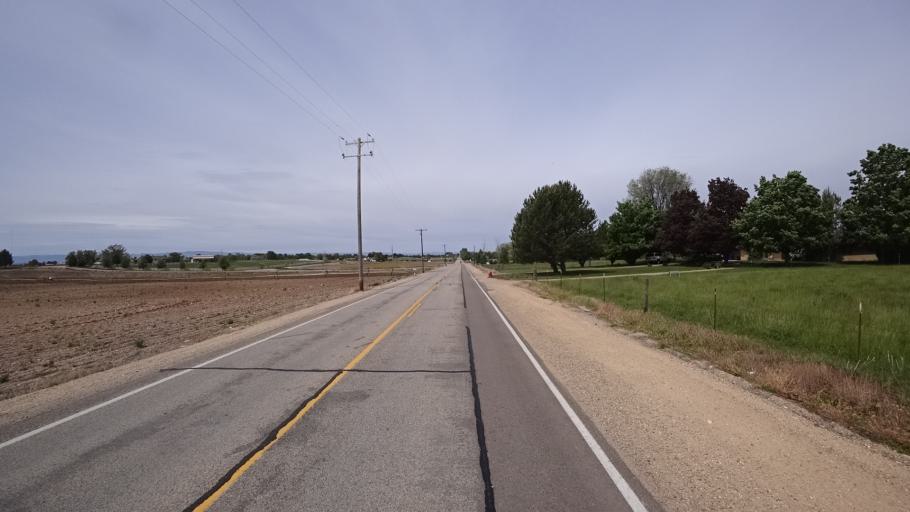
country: US
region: Idaho
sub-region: Ada County
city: Meridian
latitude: 43.5609
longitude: -116.4021
